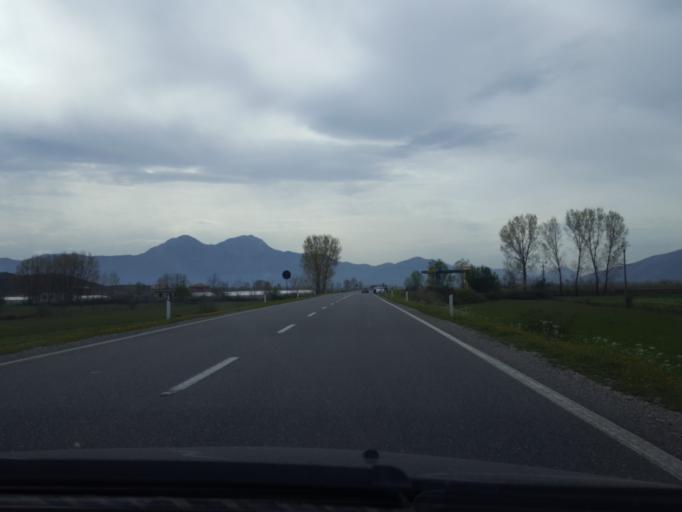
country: AL
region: Lezhe
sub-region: Rrethi i Lezhes
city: Dajc
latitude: 41.9111
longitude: 19.5986
